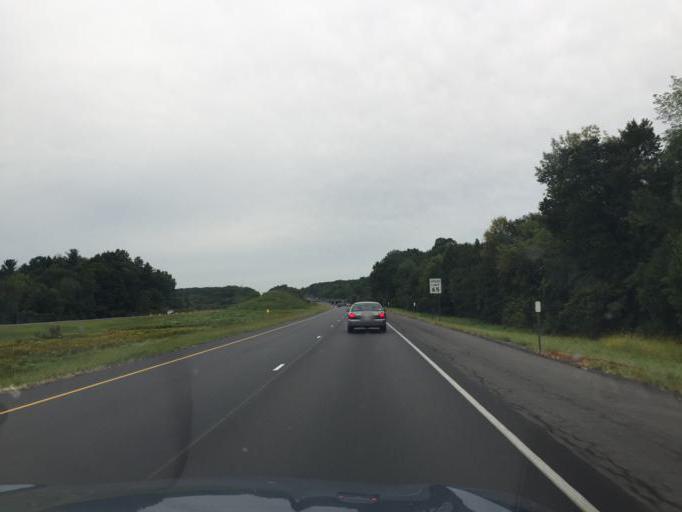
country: US
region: New York
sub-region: Rensselaer County
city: Nassau
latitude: 42.4840
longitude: -73.6390
